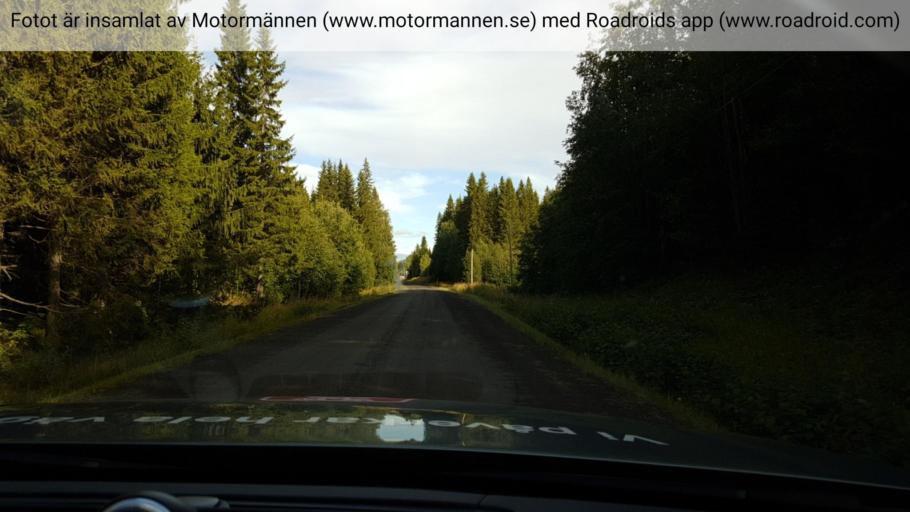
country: SE
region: Jaemtland
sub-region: Stroemsunds Kommun
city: Stroemsund
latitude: 64.1381
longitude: 15.7509
